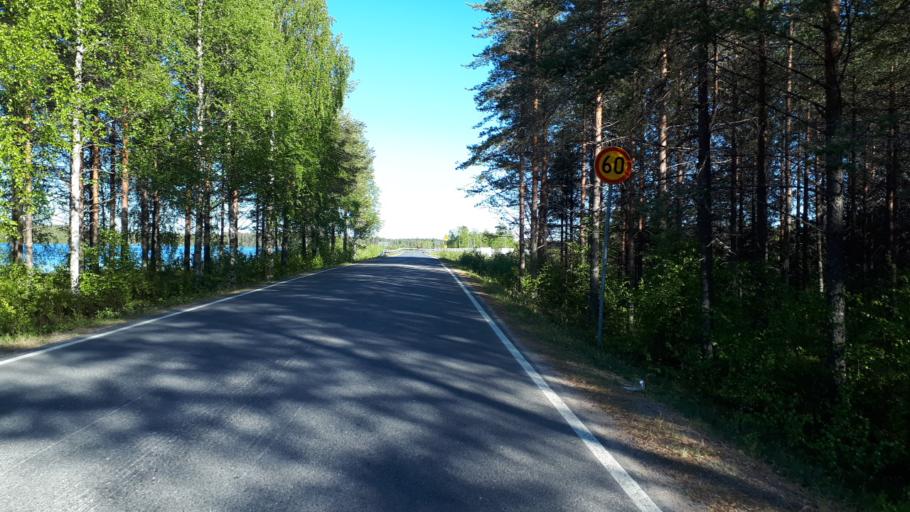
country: FI
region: Northern Ostrobothnia
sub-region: Oulunkaari
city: Ii
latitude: 65.3265
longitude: 25.5207
